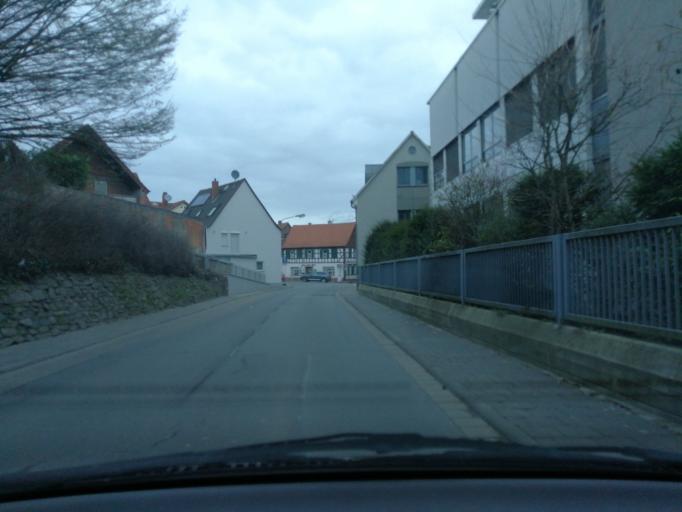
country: DE
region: Hesse
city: Reinheim
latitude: 49.8243
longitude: 8.8321
